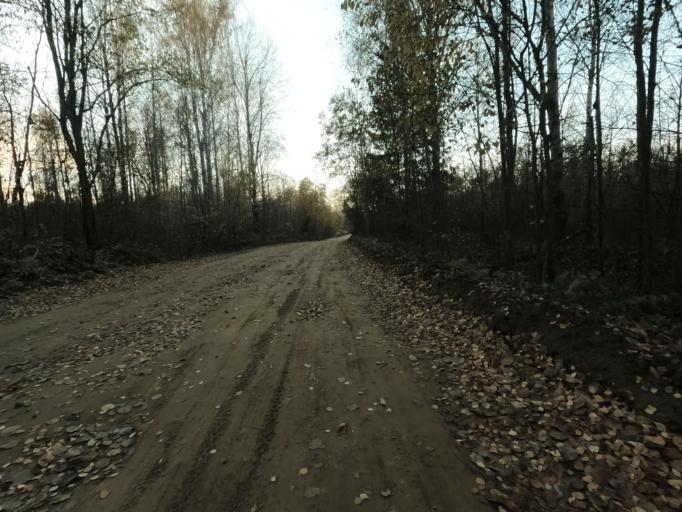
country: RU
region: Leningrad
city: Mga
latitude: 59.7554
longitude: 31.2789
